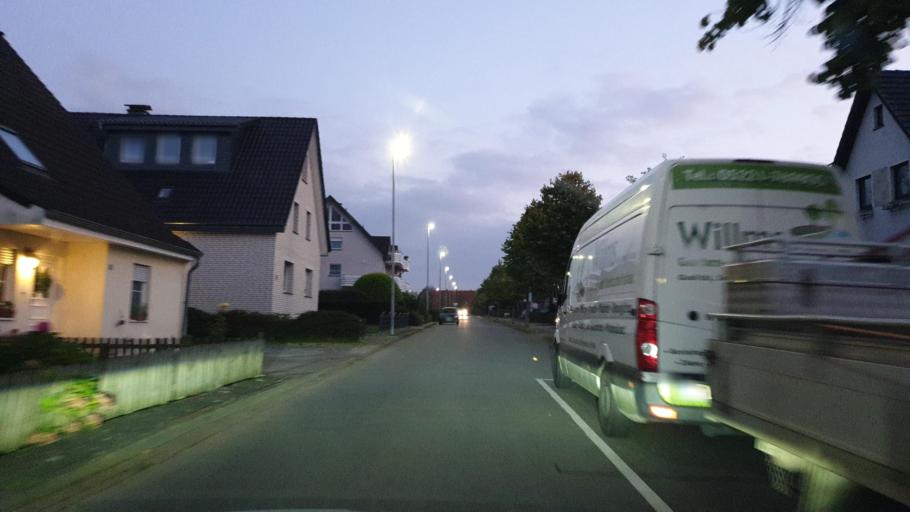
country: DE
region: North Rhine-Westphalia
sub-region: Regierungsbezirk Detmold
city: Hiddenhausen
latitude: 52.1590
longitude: 8.6346
